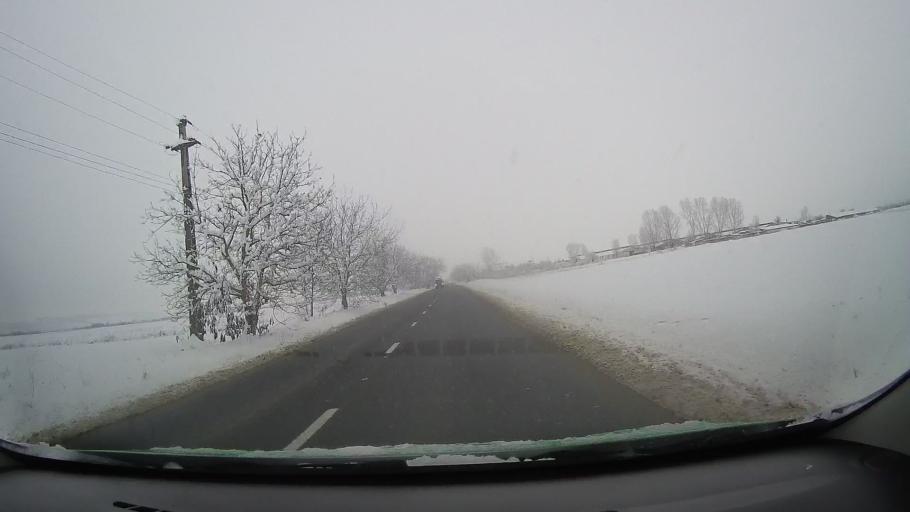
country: RO
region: Sibiu
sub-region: Comuna Orlat
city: Orlat
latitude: 45.7614
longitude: 23.9878
